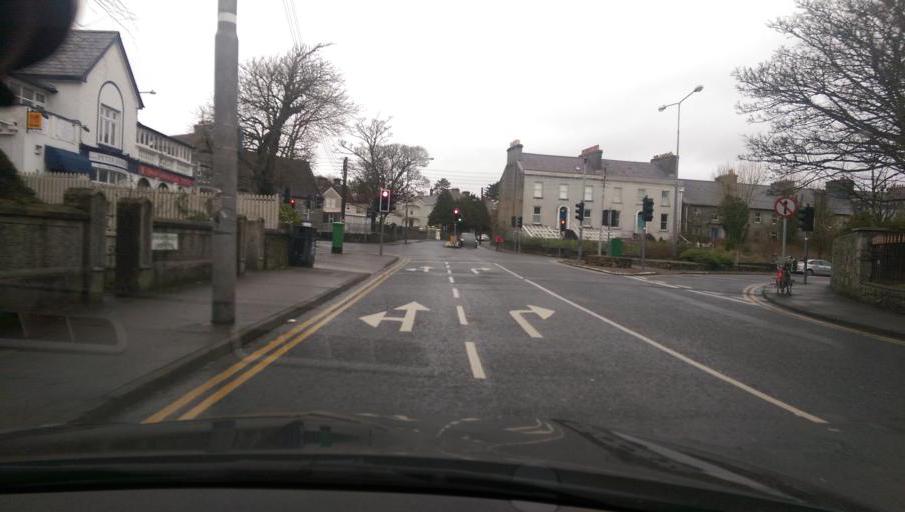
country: IE
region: Connaught
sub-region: County Galway
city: Gaillimh
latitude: 53.2684
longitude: -9.0661
